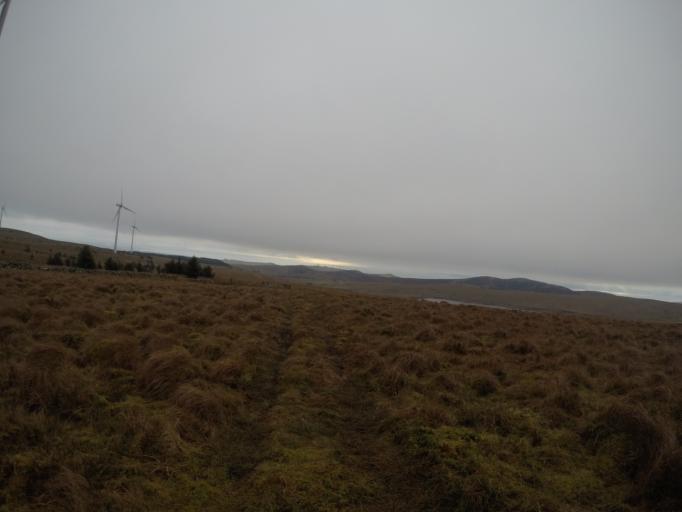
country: GB
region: Scotland
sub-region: North Ayrshire
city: Fairlie
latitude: 55.7370
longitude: -4.7903
